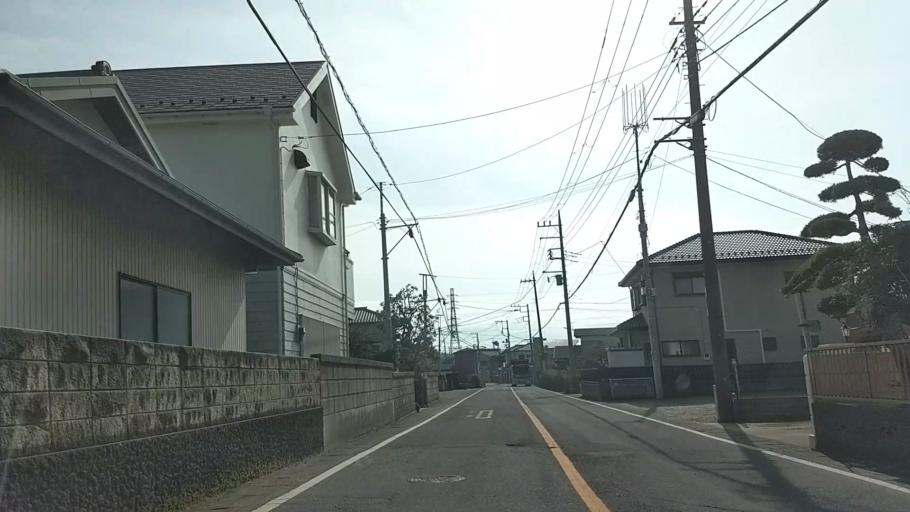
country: JP
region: Kanagawa
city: Chigasaki
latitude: 35.3548
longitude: 139.3848
